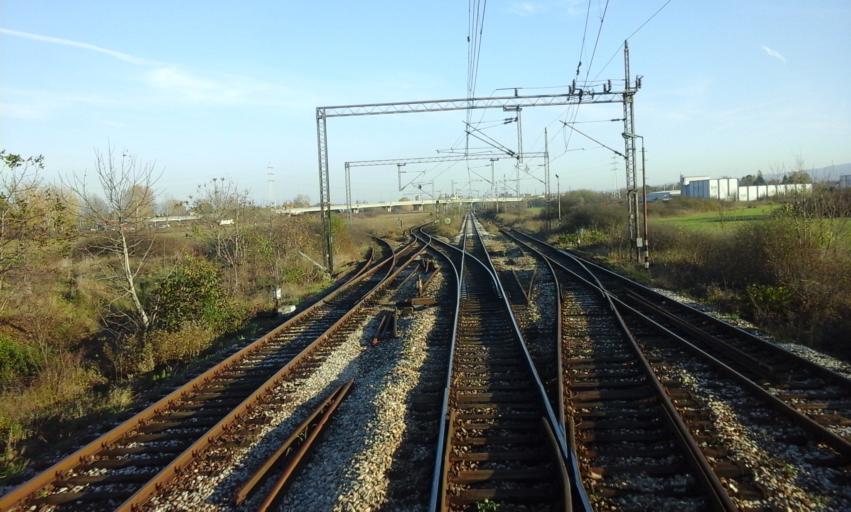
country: RS
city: Veternik
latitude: 45.2824
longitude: 19.7940
